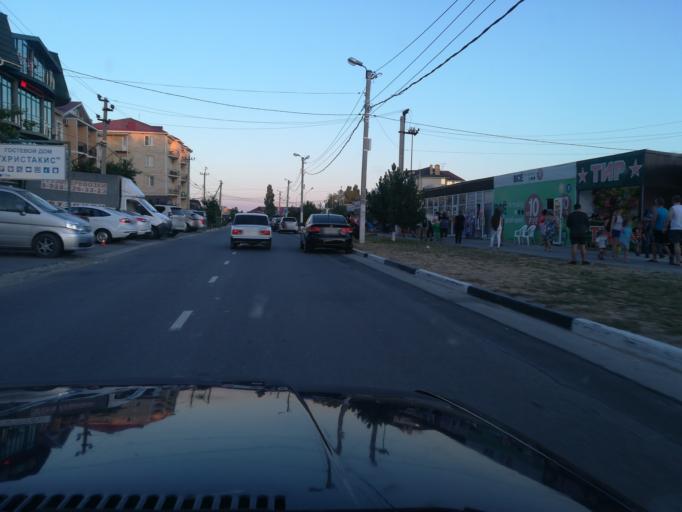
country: RU
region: Krasnodarskiy
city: Vityazevo
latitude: 44.9863
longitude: 37.2590
